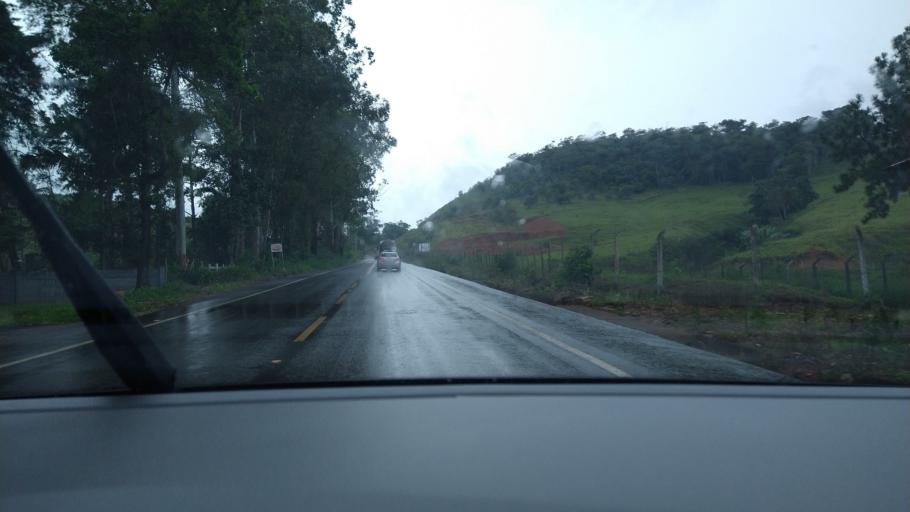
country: BR
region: Minas Gerais
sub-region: Vicosa
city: Vicosa
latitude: -20.6206
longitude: -42.8683
